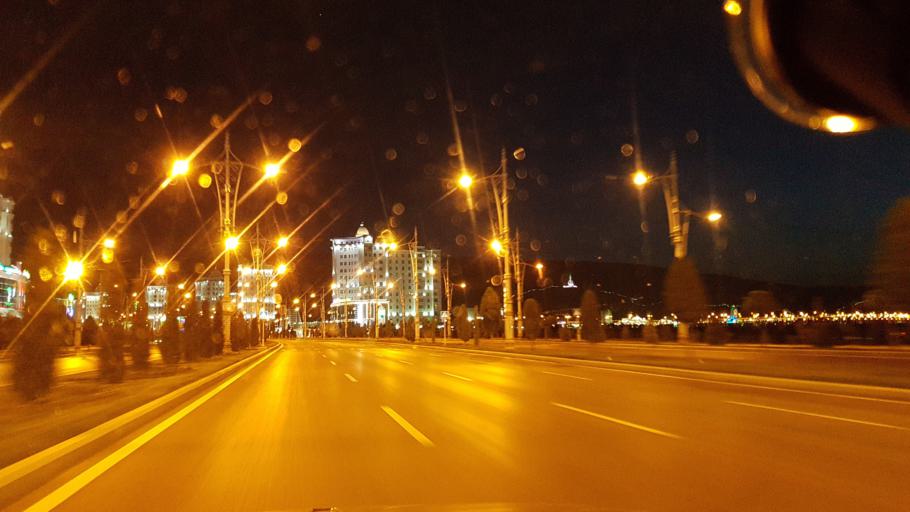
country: TM
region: Ahal
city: Ashgabat
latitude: 37.9094
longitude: 58.3388
